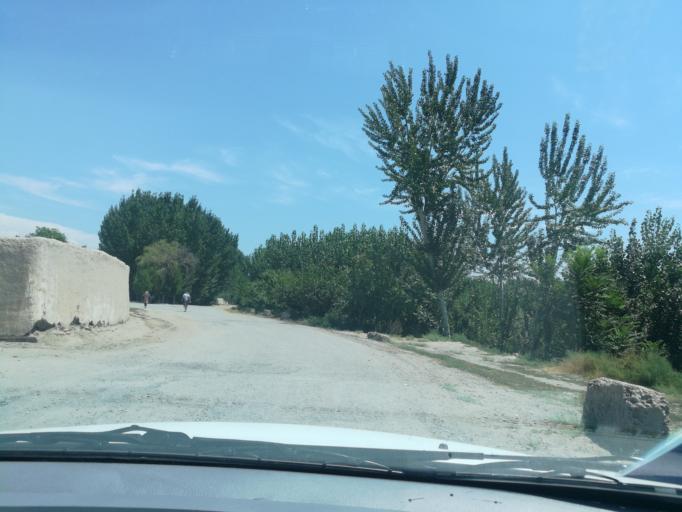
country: UZ
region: Namangan
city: Haqqulobod
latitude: 40.9022
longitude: 71.9670
